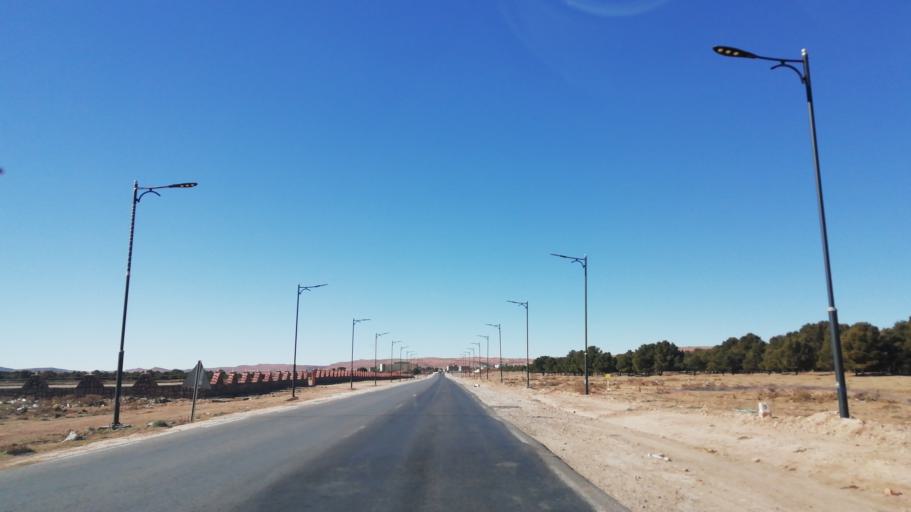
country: DZ
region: El Bayadh
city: El Bayadh
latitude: 33.7296
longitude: 1.5489
